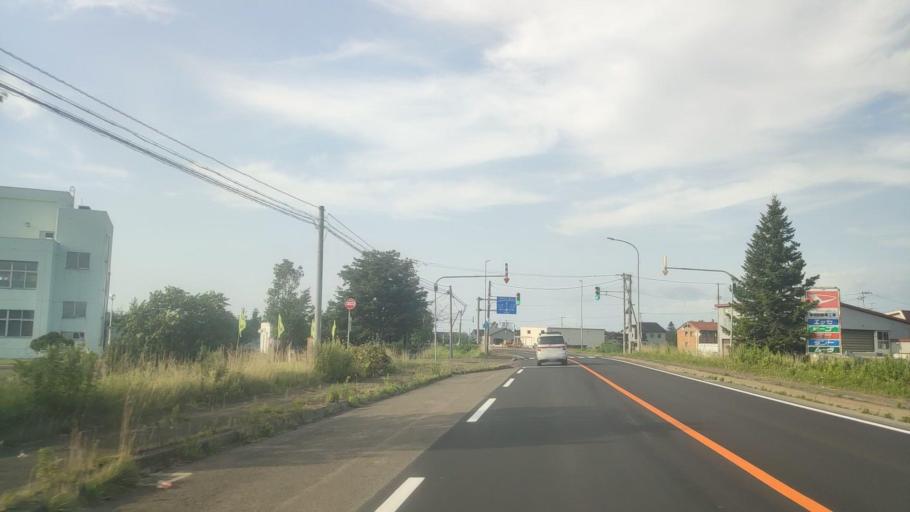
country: JP
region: Hokkaido
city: Iwamizawa
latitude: 43.0048
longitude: 141.7894
